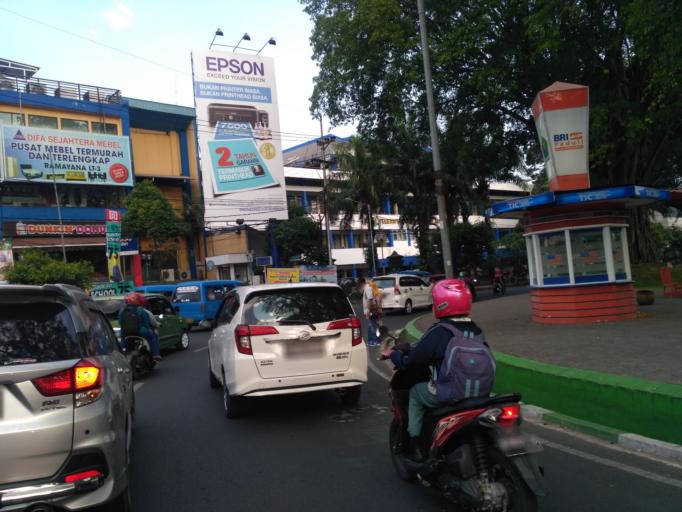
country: ID
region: East Java
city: Malang
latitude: -7.9820
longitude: 112.6315
